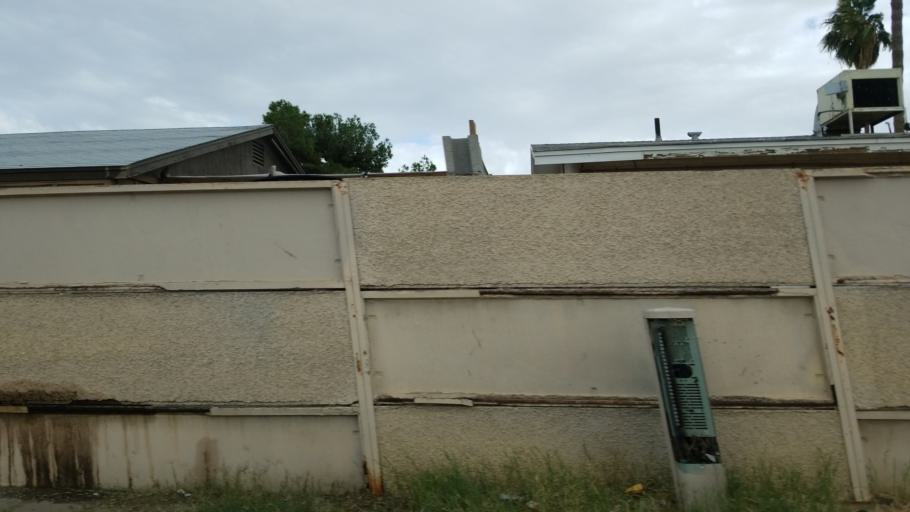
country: US
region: Arizona
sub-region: Maricopa County
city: Glendale
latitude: 33.4738
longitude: -112.1863
